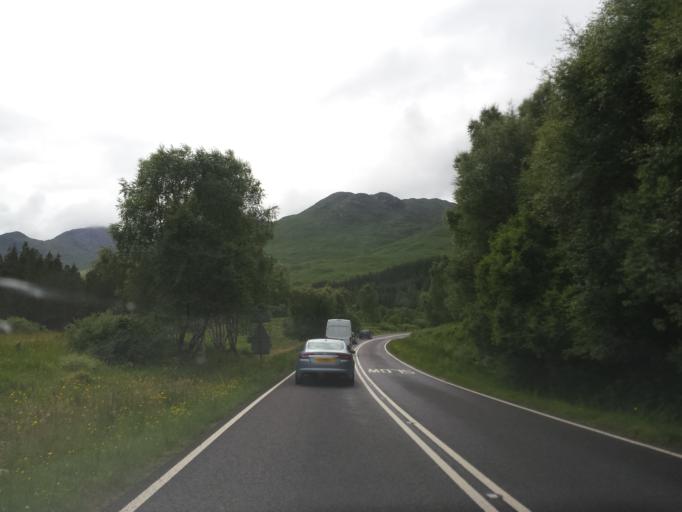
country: GB
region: Scotland
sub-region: Highland
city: Fort William
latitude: 56.8604
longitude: -5.4022
